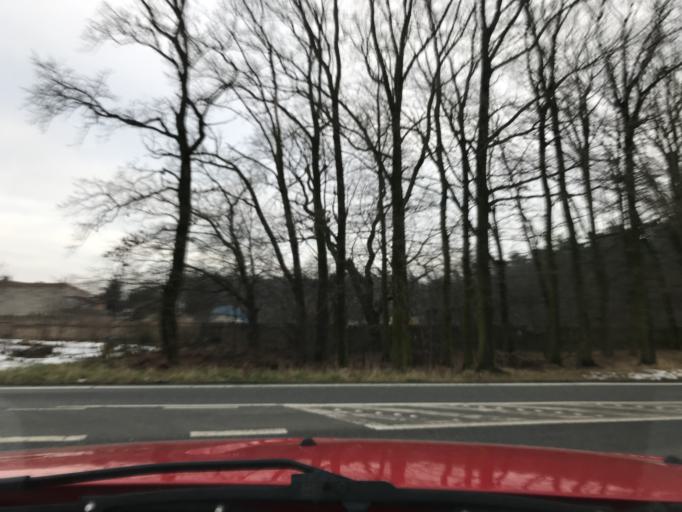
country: PL
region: Greater Poland Voivodeship
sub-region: Powiat pleszewski
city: Goluchow
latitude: 51.8472
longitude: 17.9381
